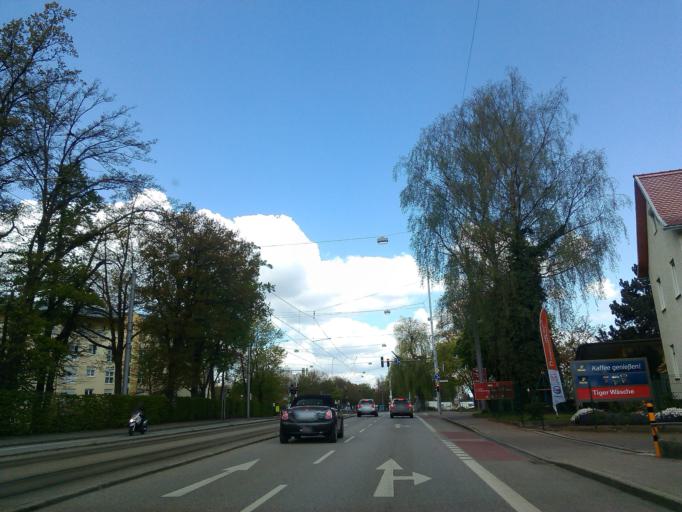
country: DE
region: Bavaria
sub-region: Swabia
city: Stadtbergen
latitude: 48.3815
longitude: 10.8481
